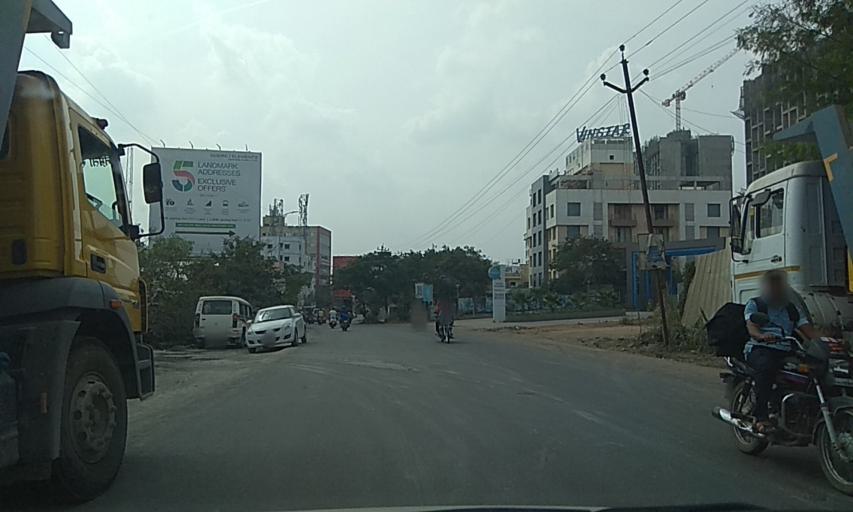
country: IN
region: Maharashtra
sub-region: Pune Division
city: Pimpri
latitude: 18.5845
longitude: 73.7310
